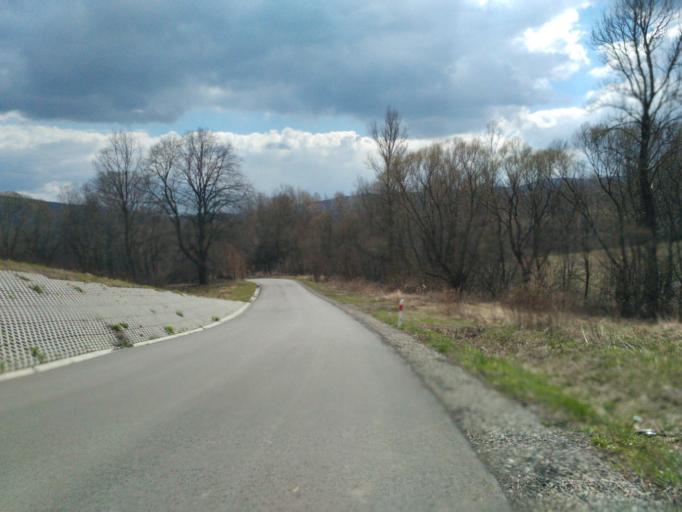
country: PL
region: Subcarpathian Voivodeship
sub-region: Powiat sanocki
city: Sanok
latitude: 49.6311
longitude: 22.2609
